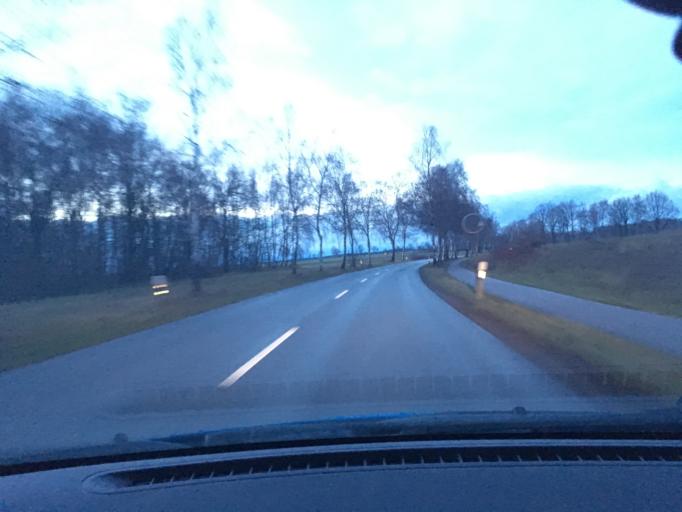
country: DE
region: Lower Saxony
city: Embsen
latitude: 53.1812
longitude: 10.3347
